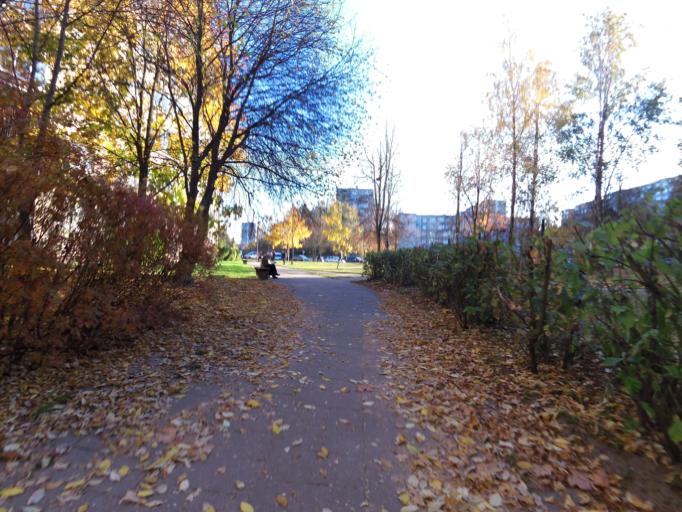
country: LT
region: Vilnius County
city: Justiniskes
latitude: 54.7210
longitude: 25.2285
